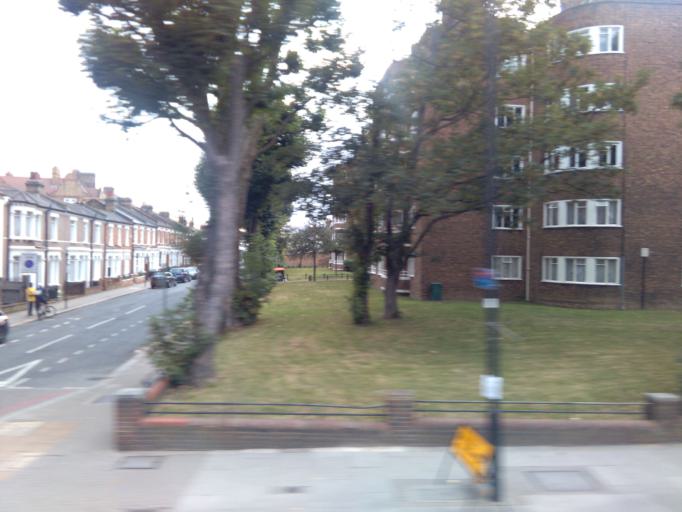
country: GB
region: England
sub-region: Greater London
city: Brixton Hill
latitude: 51.4491
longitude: -0.1482
